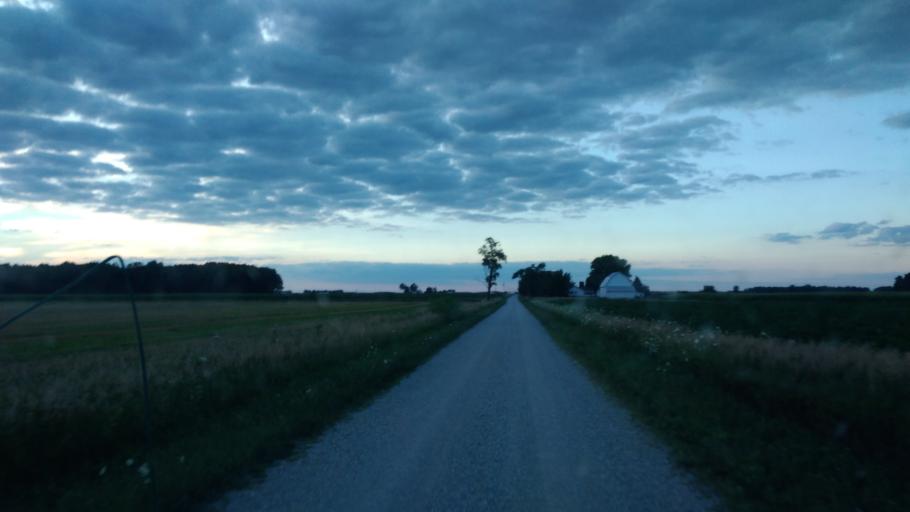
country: US
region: Indiana
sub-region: Adams County
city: Geneva
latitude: 40.6288
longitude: -85.0793
